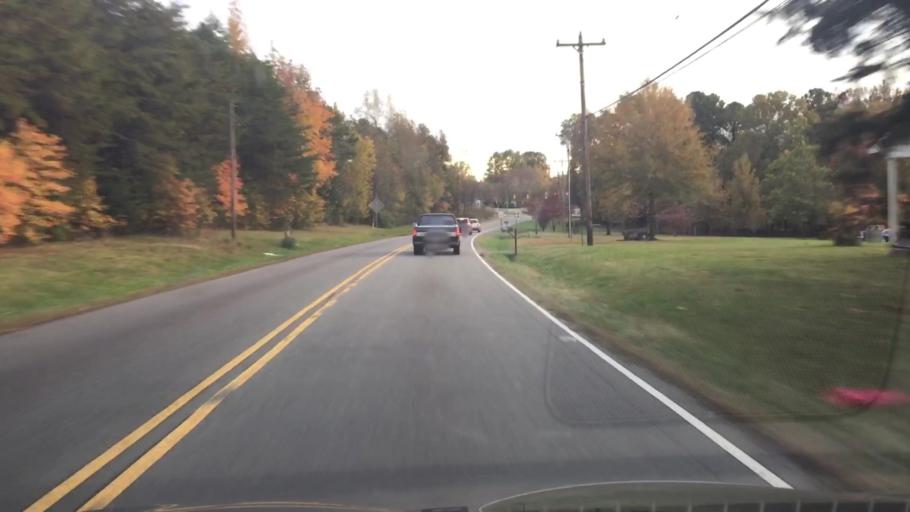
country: US
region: North Carolina
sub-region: Iredell County
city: Mooresville
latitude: 35.6277
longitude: -80.8239
